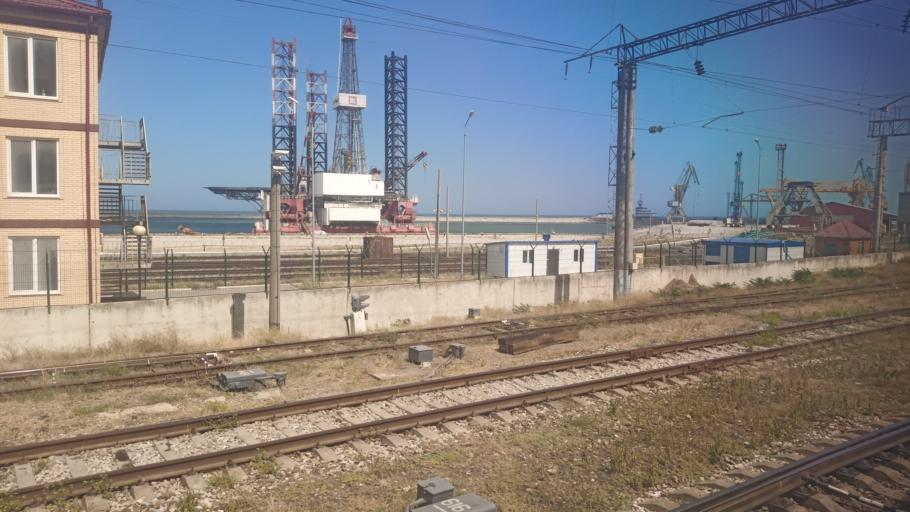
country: RU
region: Dagestan
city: Makhachkala
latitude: 42.9912
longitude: 47.4959
